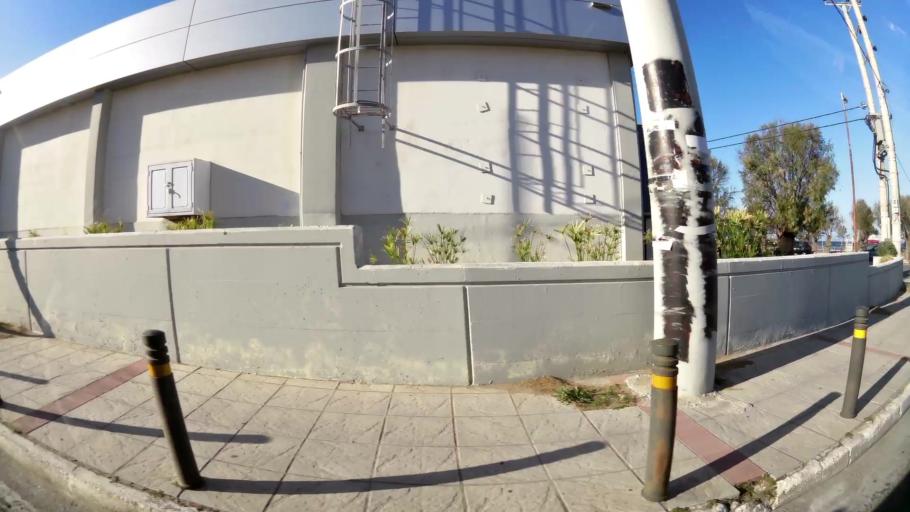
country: GR
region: Attica
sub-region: Nomarchia Anatolikis Attikis
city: Rafina
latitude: 38.0181
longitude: 24.0106
